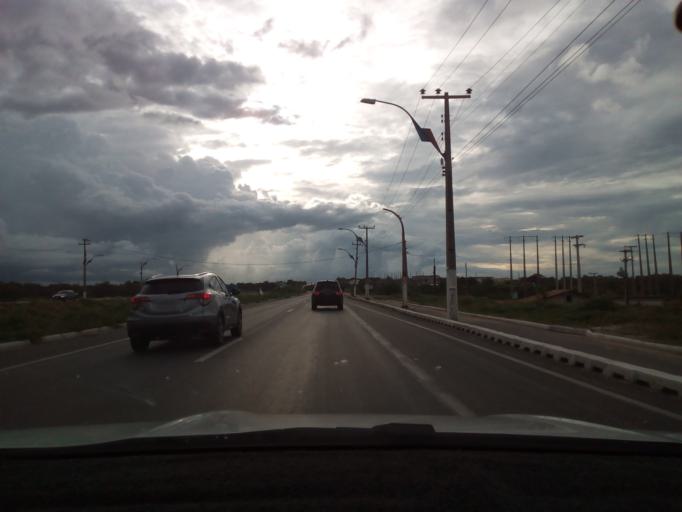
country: BR
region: Ceara
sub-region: Aracati
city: Aracati
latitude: -4.5779
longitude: -37.7824
